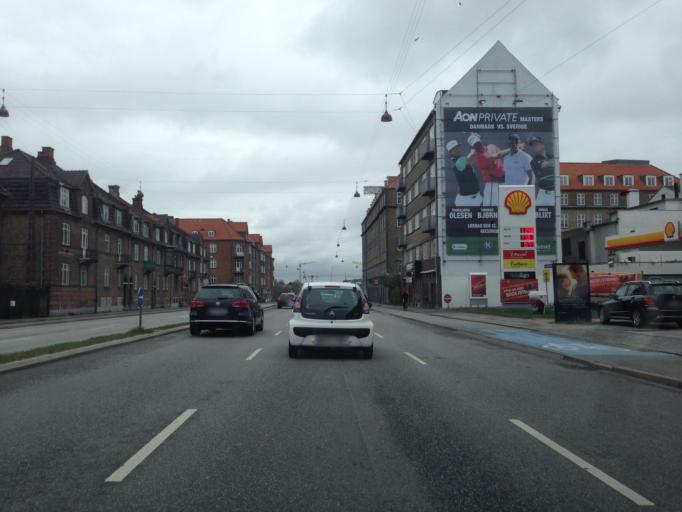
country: DK
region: Capital Region
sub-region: Kobenhavn
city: Copenhagen
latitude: 55.7110
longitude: 12.5606
